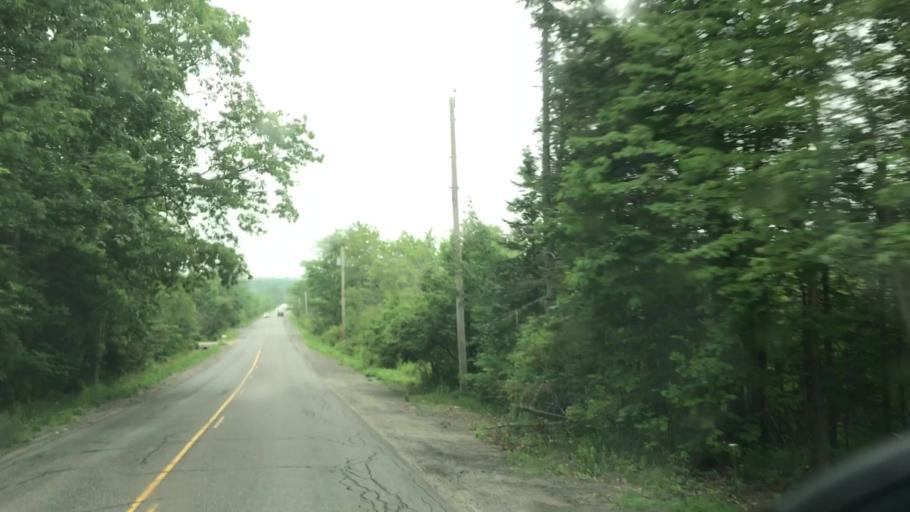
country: US
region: Maine
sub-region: Penobscot County
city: Veazie
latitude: 44.8751
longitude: -68.7136
